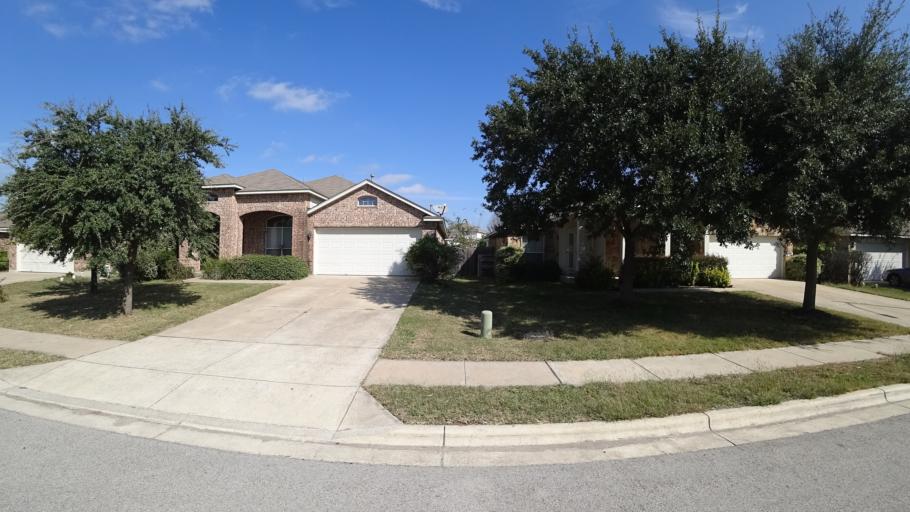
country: US
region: Texas
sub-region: Travis County
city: Pflugerville
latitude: 30.4188
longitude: -97.6338
